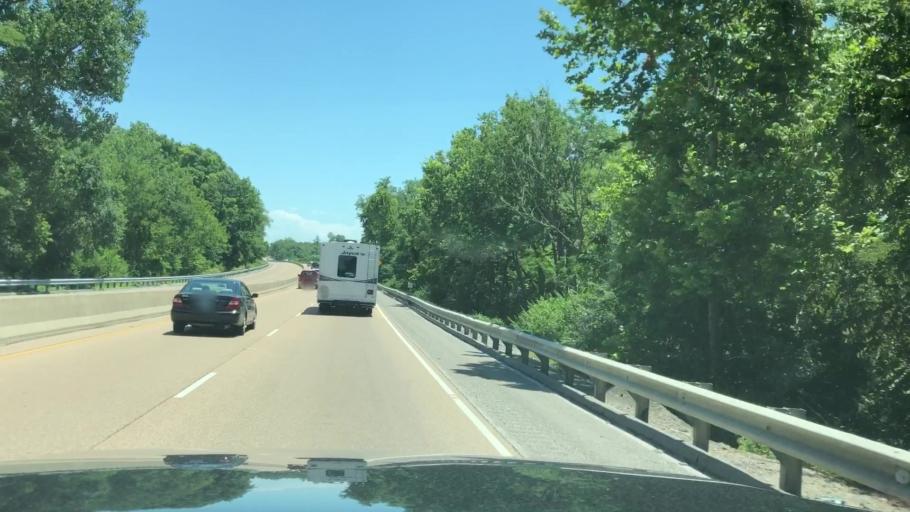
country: US
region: Illinois
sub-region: Saint Clair County
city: Alorton
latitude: 38.5582
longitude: -90.0813
